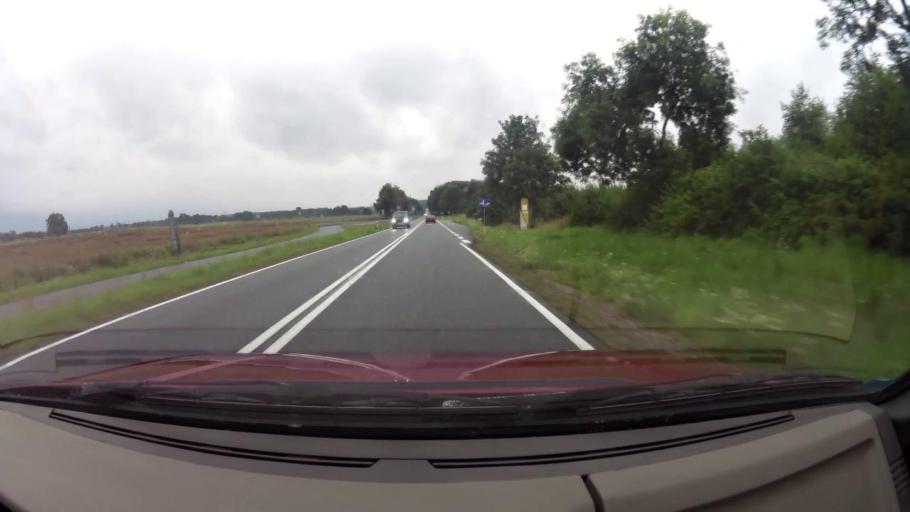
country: PL
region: West Pomeranian Voivodeship
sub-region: Powiat stargardzki
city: Chociwel
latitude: 53.4322
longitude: 15.2942
